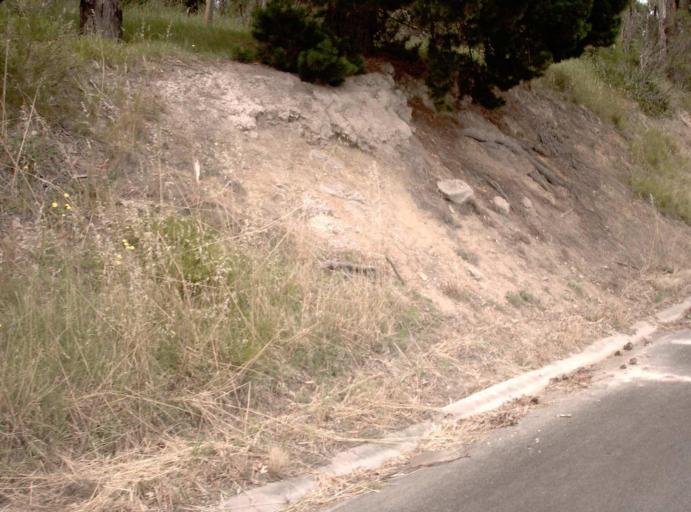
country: AU
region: Victoria
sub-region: Baw Baw
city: Warragul
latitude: -38.4081
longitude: 146.0524
